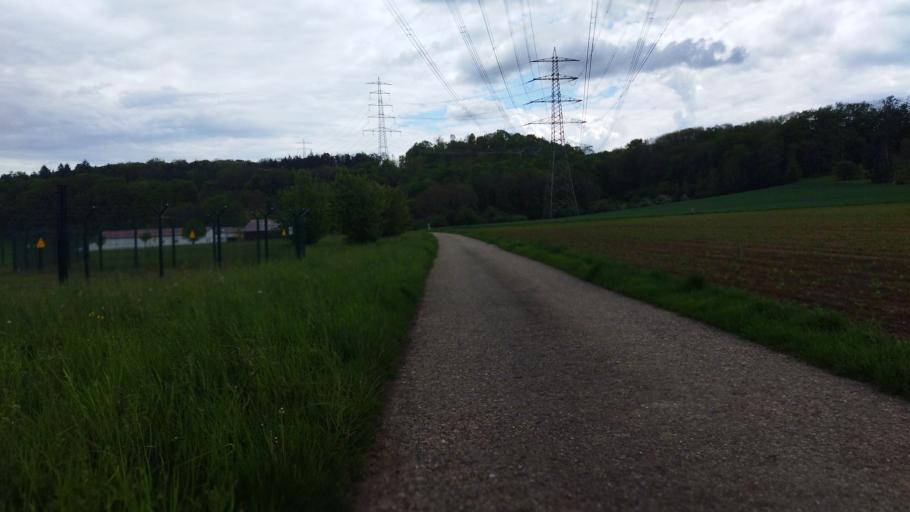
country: DE
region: Baden-Wuerttemberg
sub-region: Regierungsbezirk Stuttgart
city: Neckarwestheim
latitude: 49.0377
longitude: 9.1761
